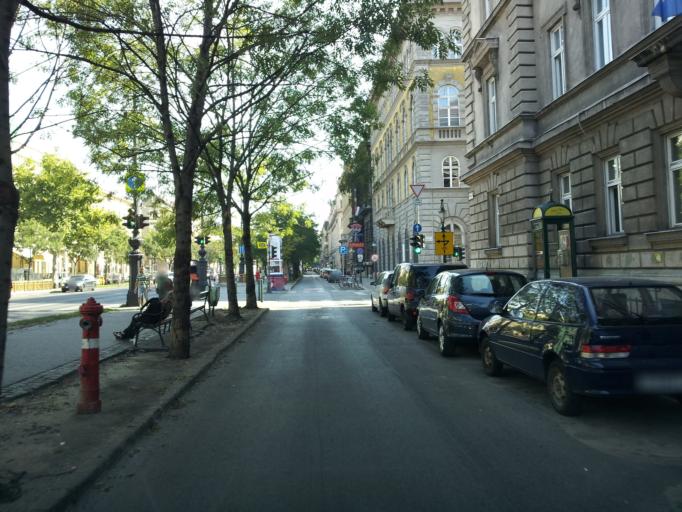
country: HU
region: Budapest
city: Budapest VI. keruelet
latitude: 47.5069
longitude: 19.0660
